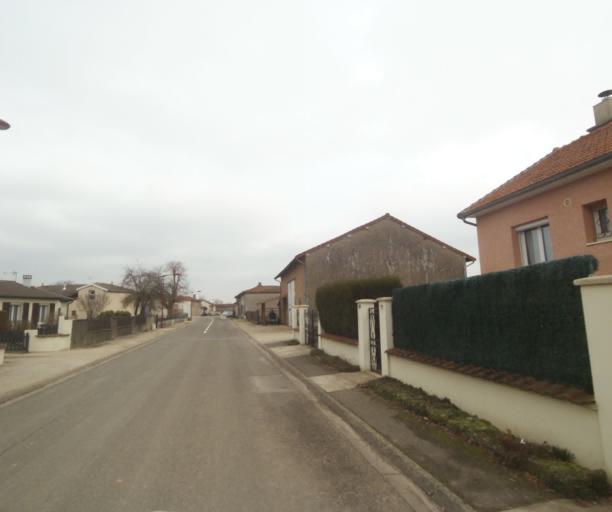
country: FR
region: Champagne-Ardenne
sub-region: Departement de la Marne
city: Pargny-sur-Saulx
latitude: 48.6936
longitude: 4.7990
